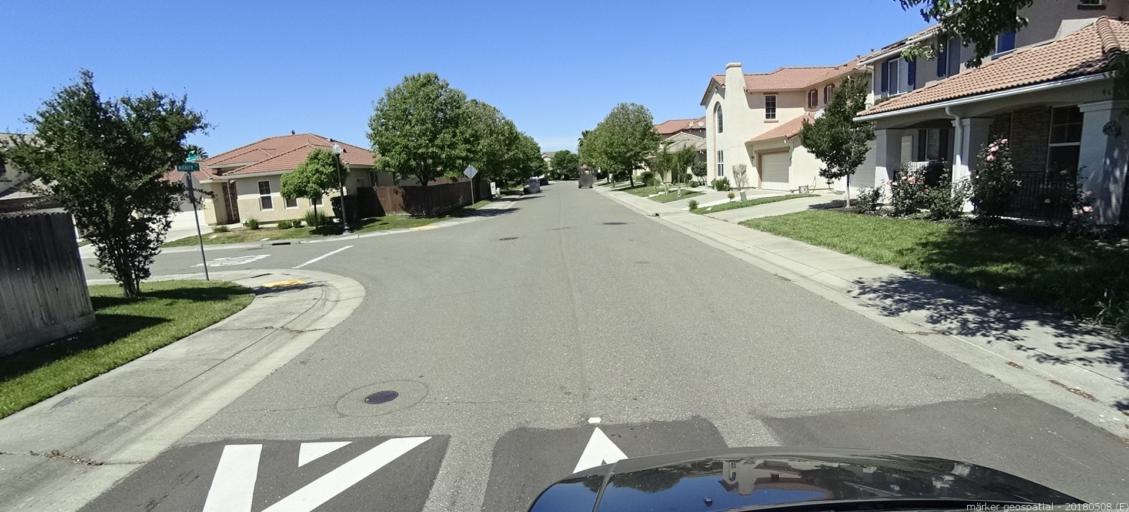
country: US
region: California
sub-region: Sacramento County
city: Elverta
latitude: 38.6832
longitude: -121.5360
